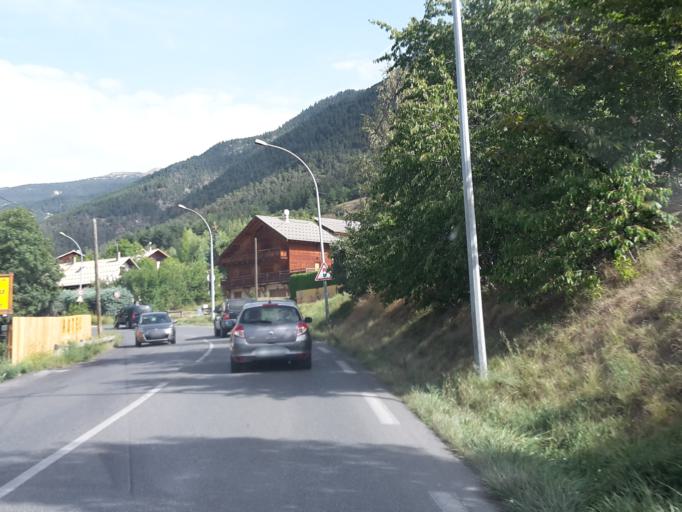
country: FR
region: Provence-Alpes-Cote d'Azur
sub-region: Departement des Hautes-Alpes
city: Saint-Chaffrey
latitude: 44.9124
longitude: 6.6240
